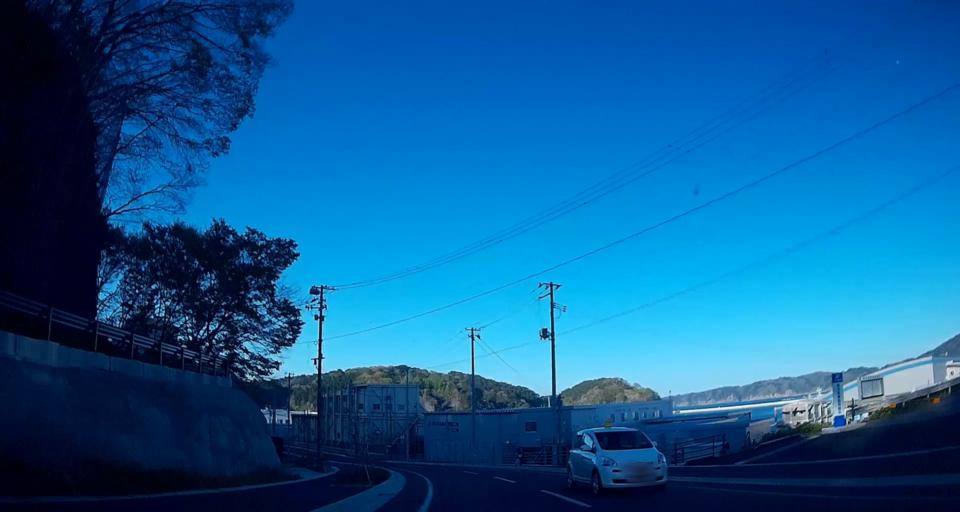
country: JP
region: Iwate
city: Miyako
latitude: 39.6408
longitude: 141.9665
